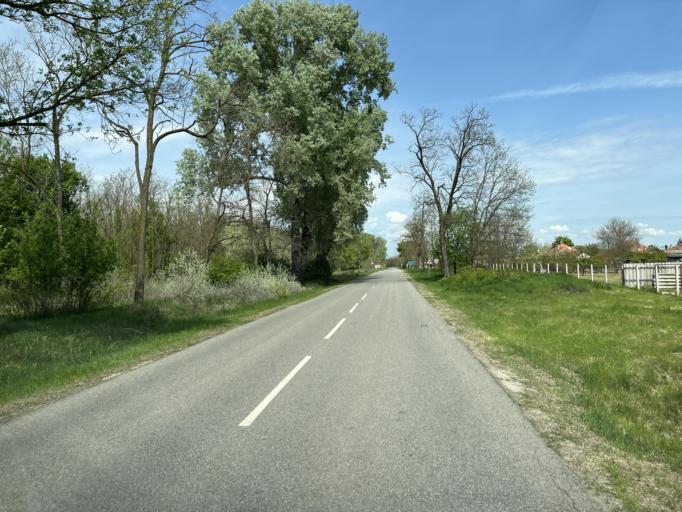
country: HU
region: Pest
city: Albertirsa
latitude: 47.1594
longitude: 19.6123
